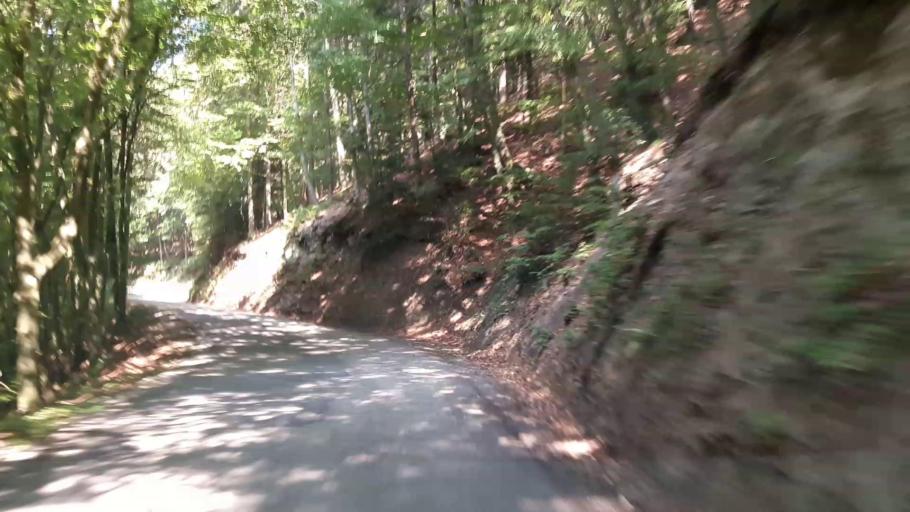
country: AT
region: Lower Austria
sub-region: Politischer Bezirk Krems
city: Aggsbach
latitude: 48.2891
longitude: 15.3763
